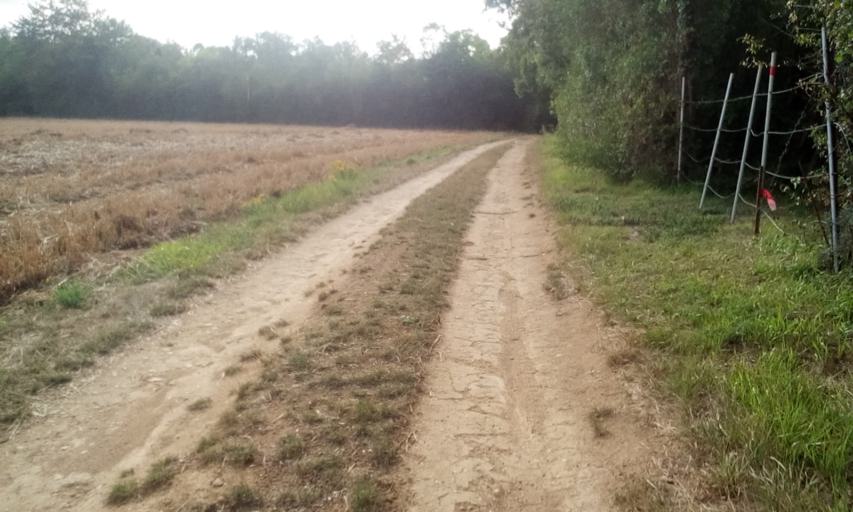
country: FR
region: Lower Normandy
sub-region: Departement du Calvados
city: Cagny
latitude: 49.1043
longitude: -0.2530
